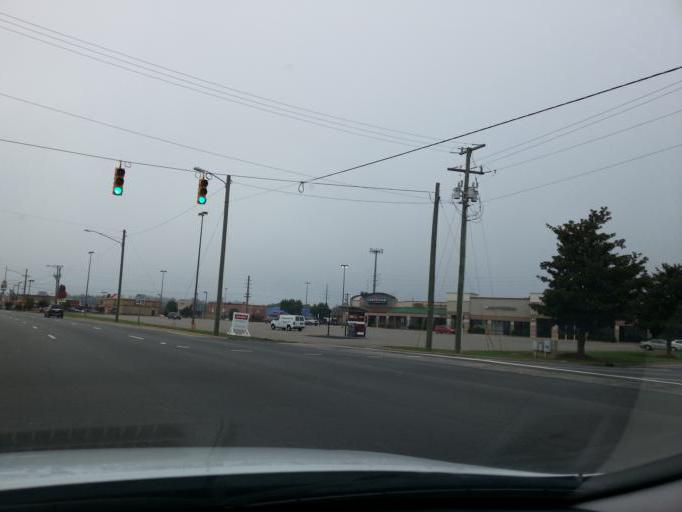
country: US
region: North Carolina
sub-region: Cumberland County
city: Fort Bragg
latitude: 35.0729
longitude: -78.9647
